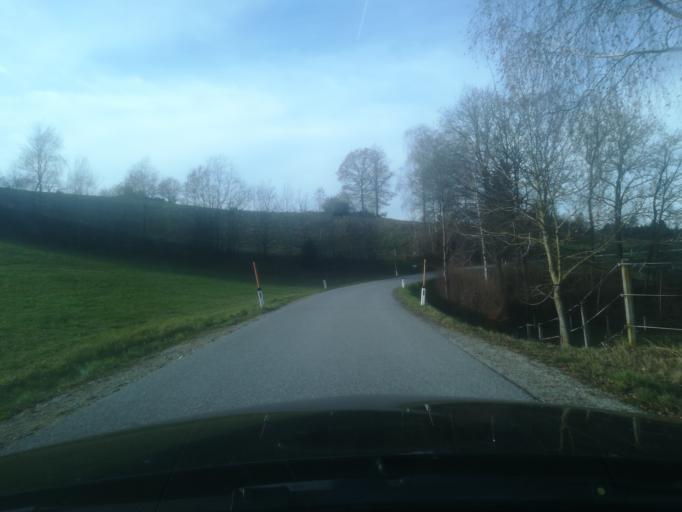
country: AT
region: Upper Austria
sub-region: Politischer Bezirk Perg
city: Perg
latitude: 48.3260
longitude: 14.6549
